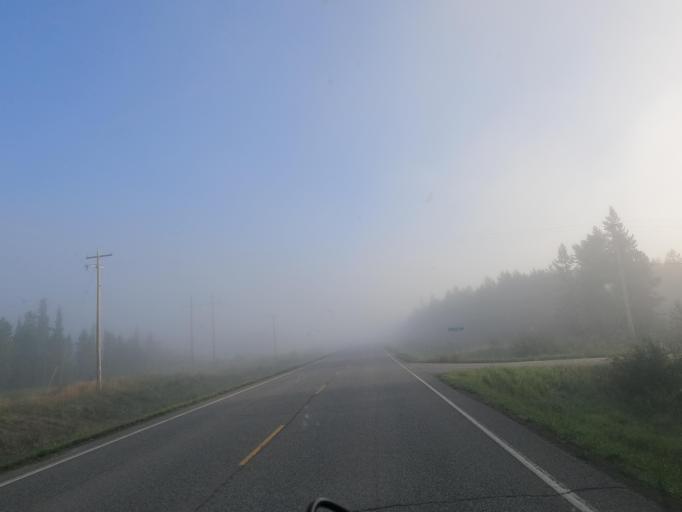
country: CA
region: Yukon
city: Whitehorse
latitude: 60.8865
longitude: -135.1848
